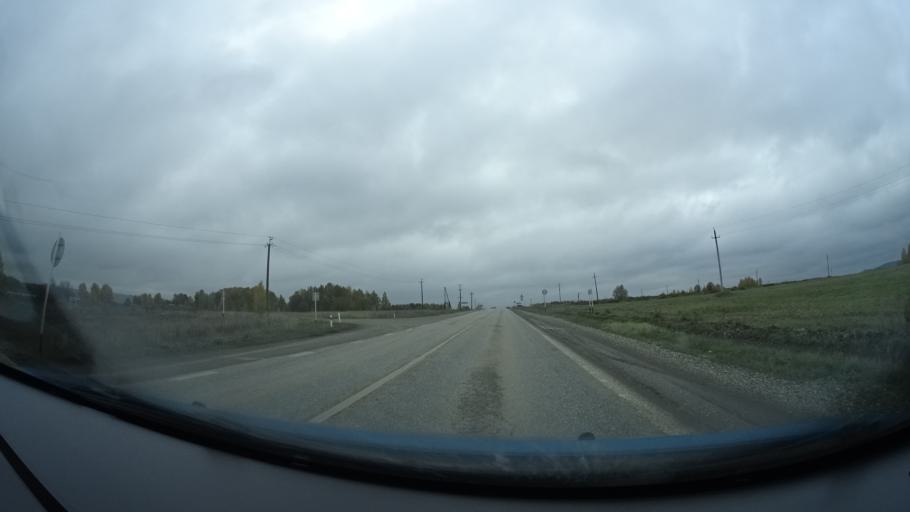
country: RU
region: Perm
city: Osa
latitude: 57.1592
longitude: 55.5303
